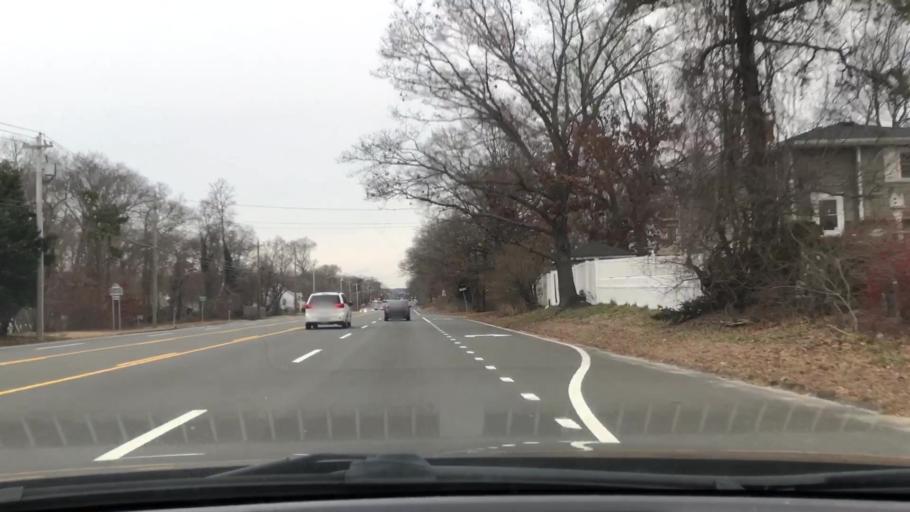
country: US
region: New York
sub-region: Suffolk County
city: North Patchogue
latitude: 40.7884
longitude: -73.0165
